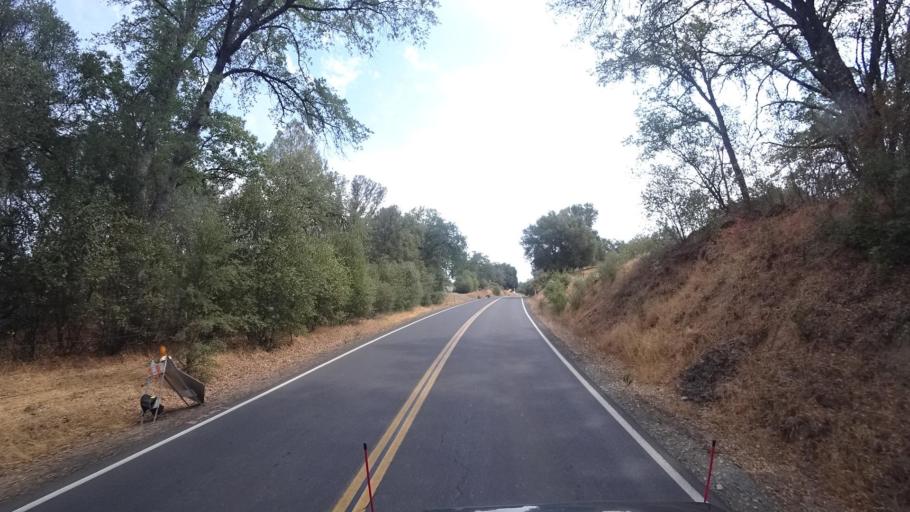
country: US
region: California
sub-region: Mariposa County
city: Midpines
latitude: 37.4714
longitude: -119.8780
